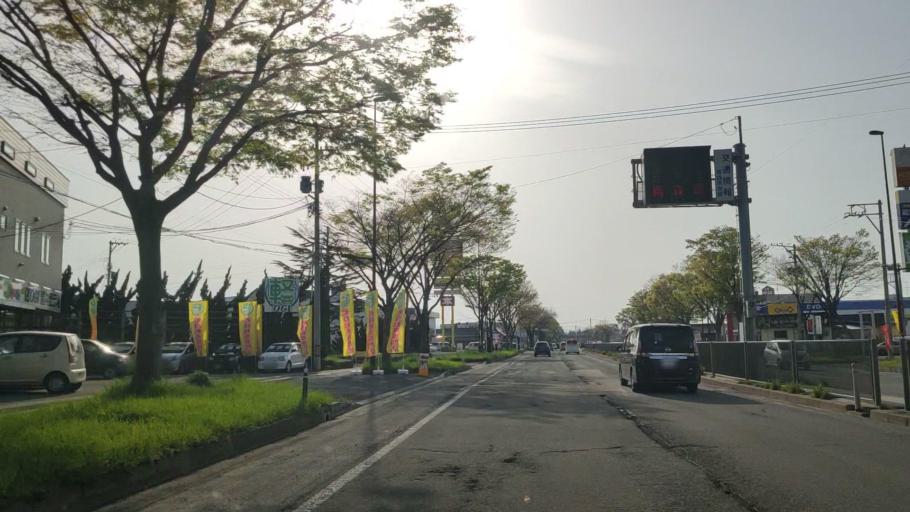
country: JP
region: Aomori
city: Aomori Shi
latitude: 40.8267
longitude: 140.7972
